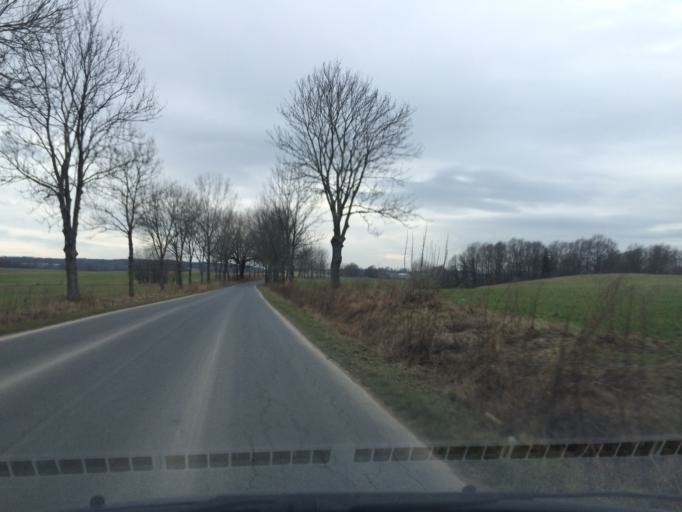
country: PL
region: Lower Silesian Voivodeship
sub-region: Powiat lwowecki
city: Lwowek Slaski
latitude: 51.1211
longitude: 15.5067
